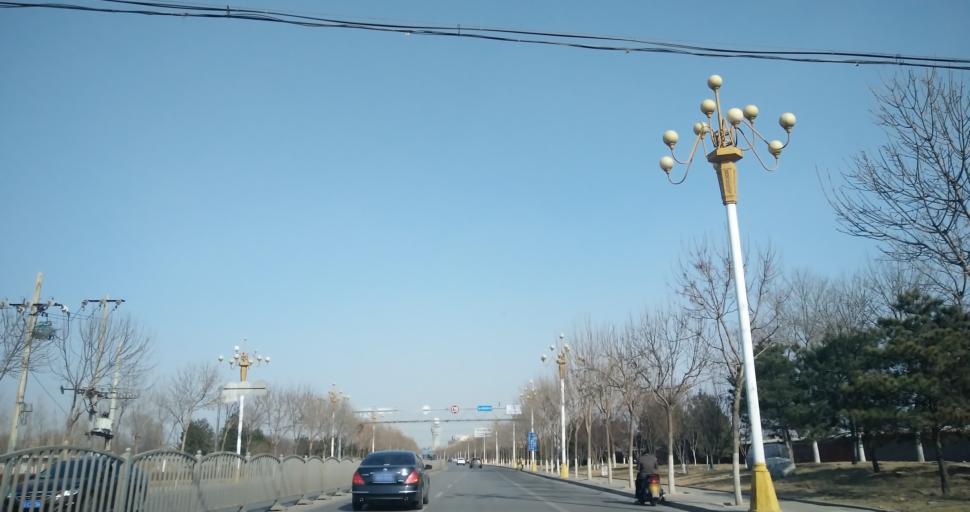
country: CN
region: Beijing
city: Jiugong
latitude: 39.8051
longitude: 116.4566
